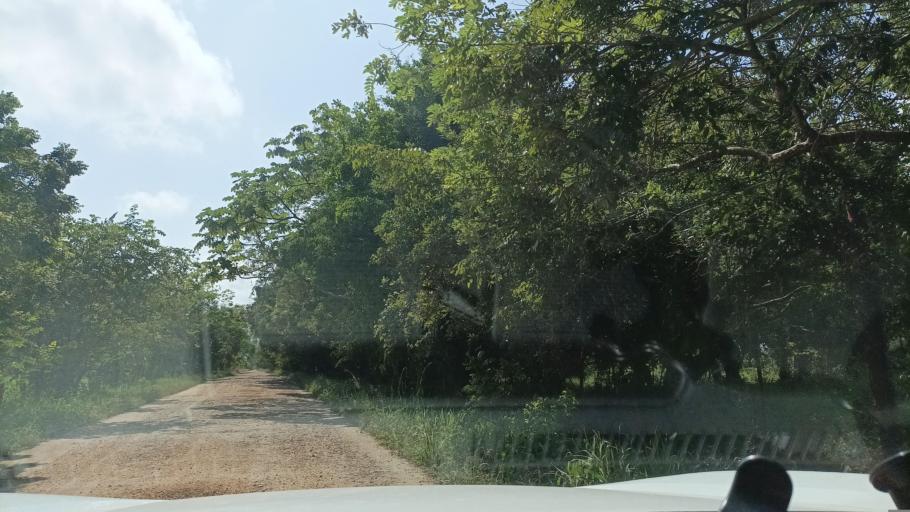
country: MX
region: Veracruz
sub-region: Chinameca
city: Chacalapa
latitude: 18.1149
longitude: -94.6631
